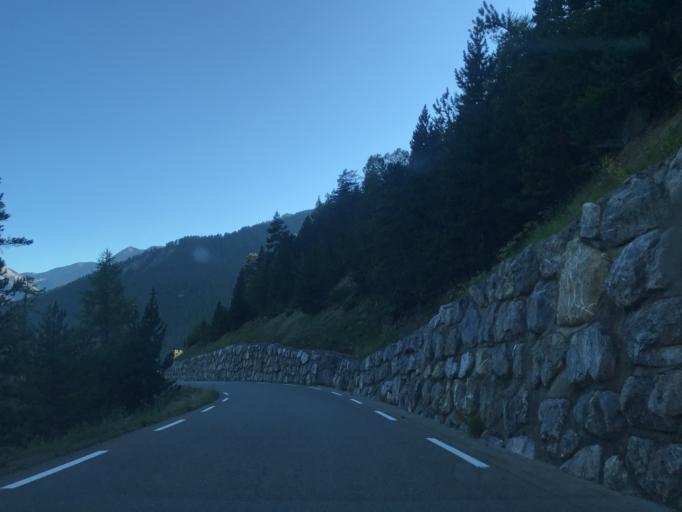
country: FR
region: Provence-Alpes-Cote d'Azur
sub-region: Departement des Hautes-Alpes
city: Villar-Saint-Pancrace
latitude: 44.7983
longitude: 6.7342
